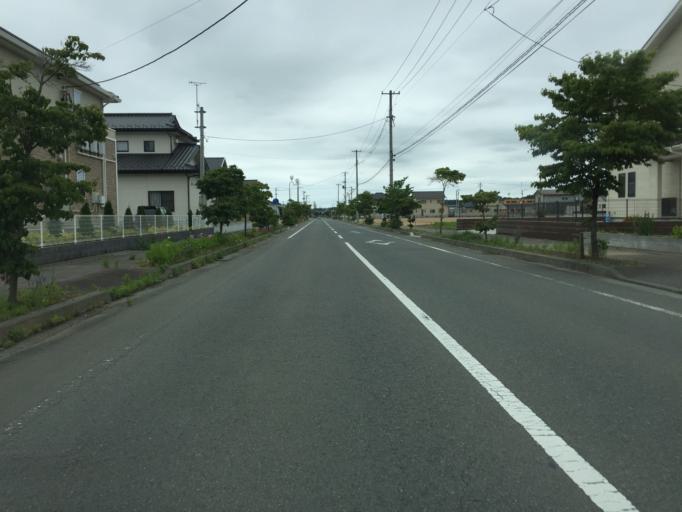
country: JP
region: Fukushima
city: Namie
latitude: 37.7109
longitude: 140.9583
